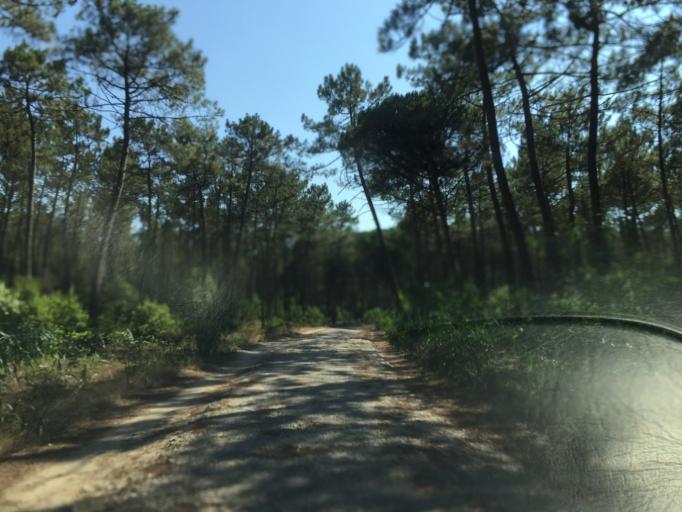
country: PT
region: Coimbra
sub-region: Figueira da Foz
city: Tavarede
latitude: 40.2487
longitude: -8.8426
